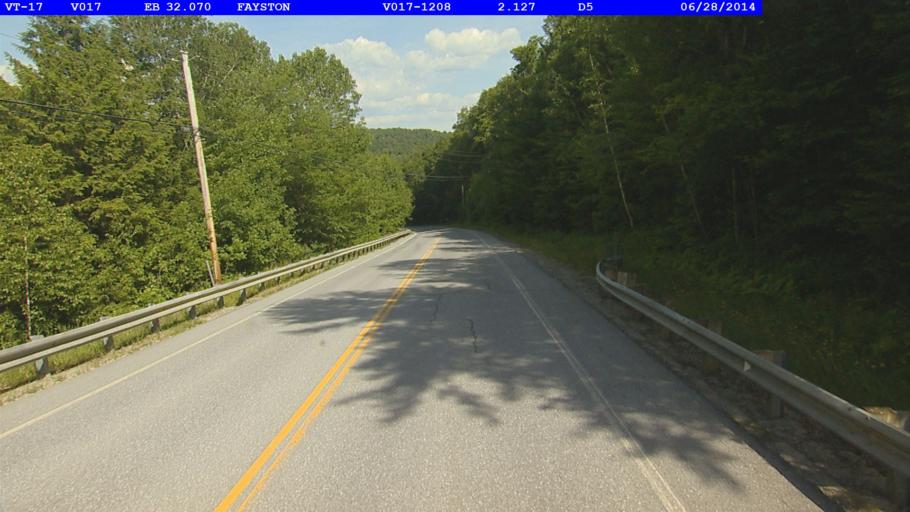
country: US
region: Vermont
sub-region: Addison County
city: Bristol
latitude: 44.2046
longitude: -72.9009
